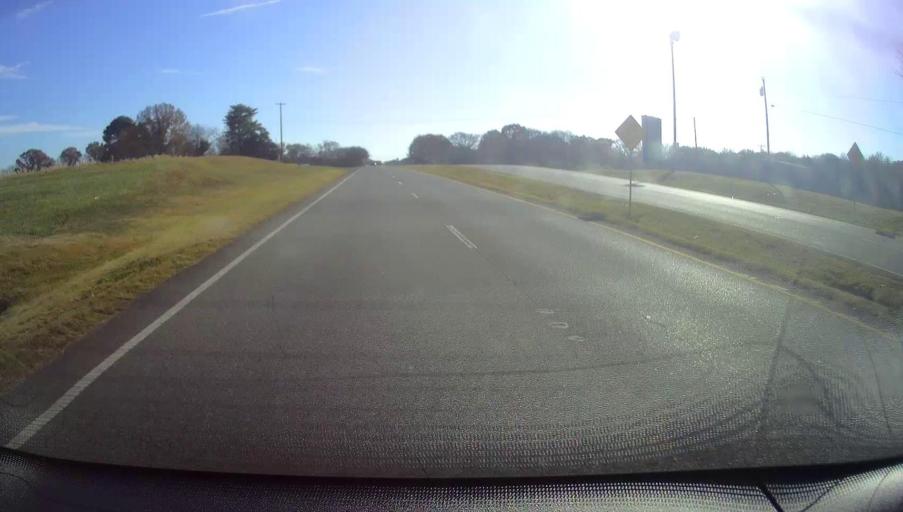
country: US
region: Alabama
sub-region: Morgan County
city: Decatur
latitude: 34.6362
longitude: -86.9507
